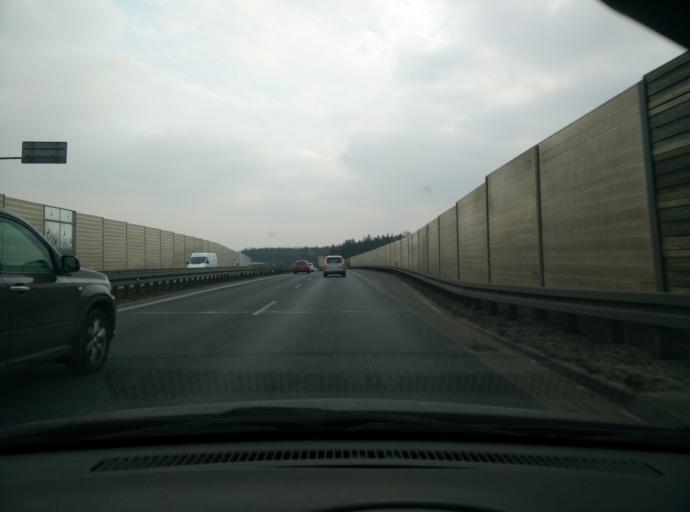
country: PL
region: Greater Poland Voivodeship
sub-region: Powiat poznanski
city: Kornik
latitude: 52.3005
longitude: 17.0489
